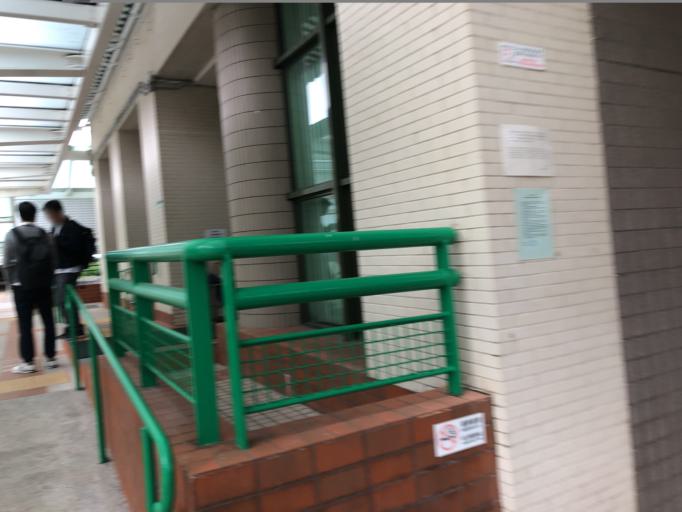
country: HK
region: Tai Po
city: Tai Po
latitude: 22.4668
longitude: 114.1937
